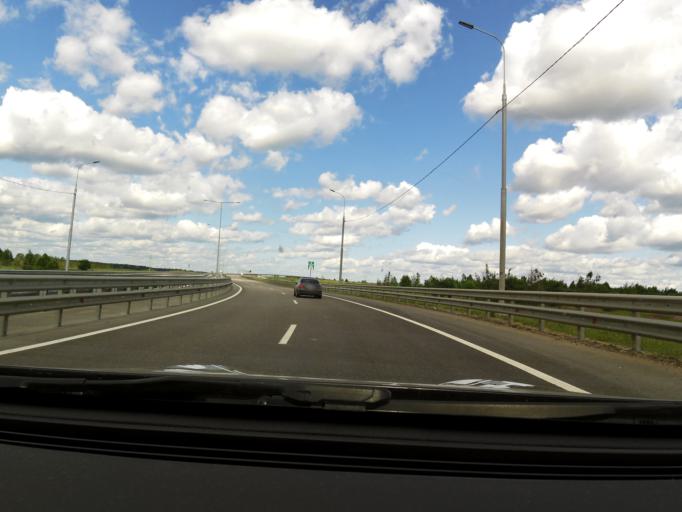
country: RU
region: Tverskaya
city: Vydropuzhsk
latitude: 57.2327
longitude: 34.9099
